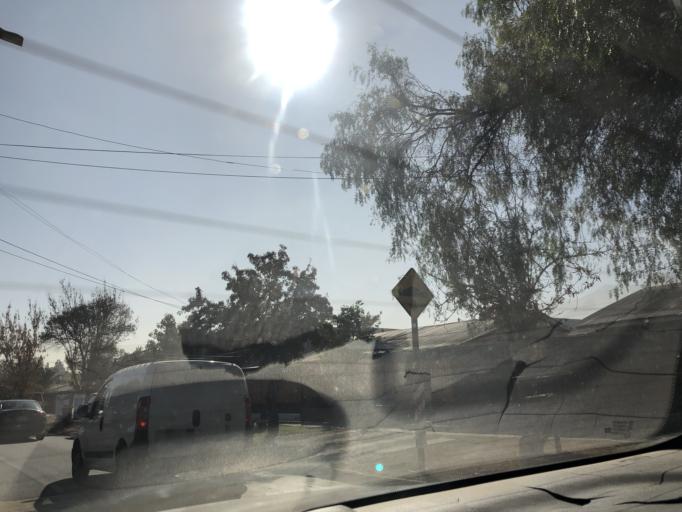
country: CL
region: Santiago Metropolitan
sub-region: Provincia de Cordillera
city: Puente Alto
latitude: -33.5814
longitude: -70.5872
